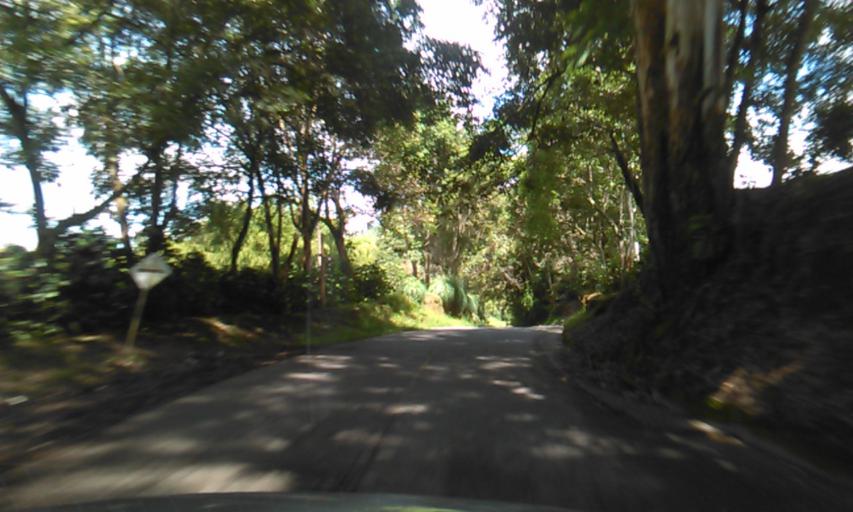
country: CO
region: Quindio
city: Cordoba
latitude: 4.3997
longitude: -75.6895
